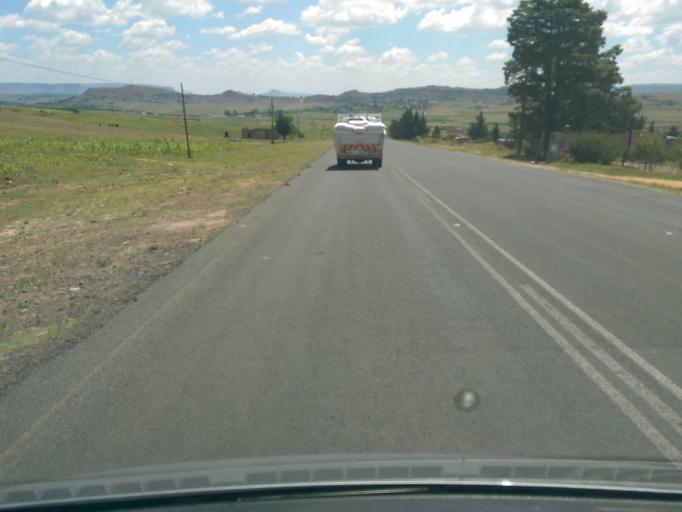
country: LS
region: Maseru
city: Nako
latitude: -29.4237
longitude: 27.6715
